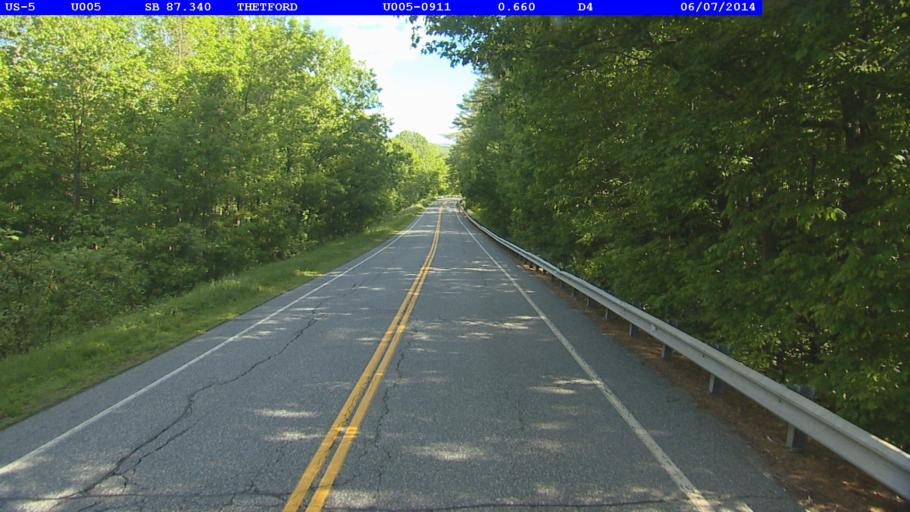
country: US
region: New Hampshire
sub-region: Grafton County
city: Lyme
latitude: 43.7812
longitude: -72.2064
